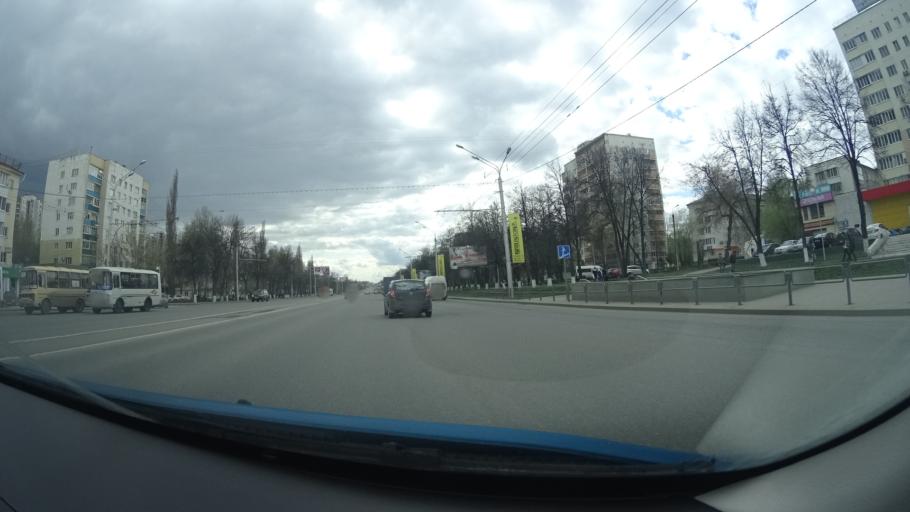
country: RU
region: Bashkortostan
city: Ufa
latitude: 54.7595
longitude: 56.0096
